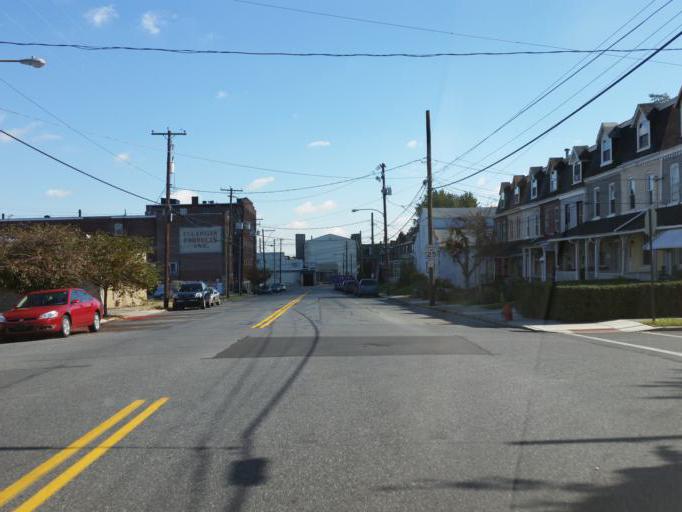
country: US
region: Pennsylvania
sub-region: Lancaster County
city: Lancaster
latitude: 40.0528
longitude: -76.3020
